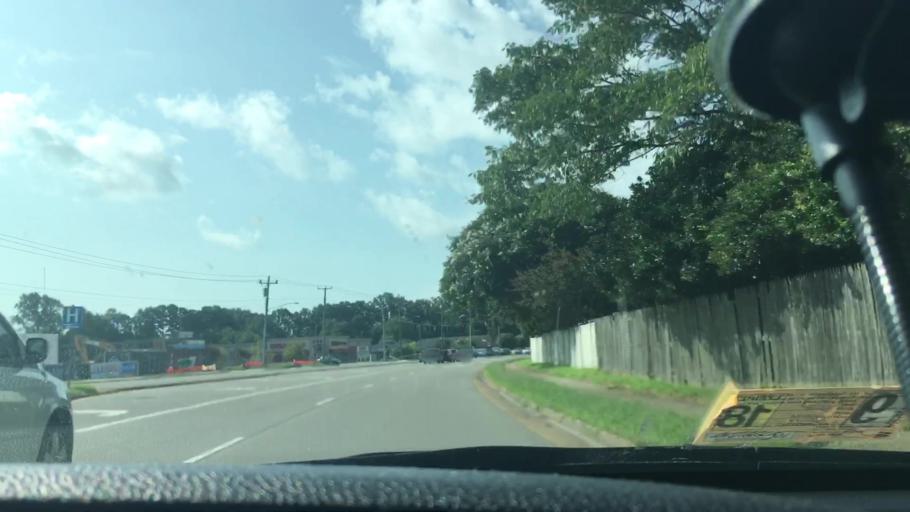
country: US
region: Virginia
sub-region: City of Virginia Beach
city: Virginia Beach
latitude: 36.8755
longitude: -76.0400
